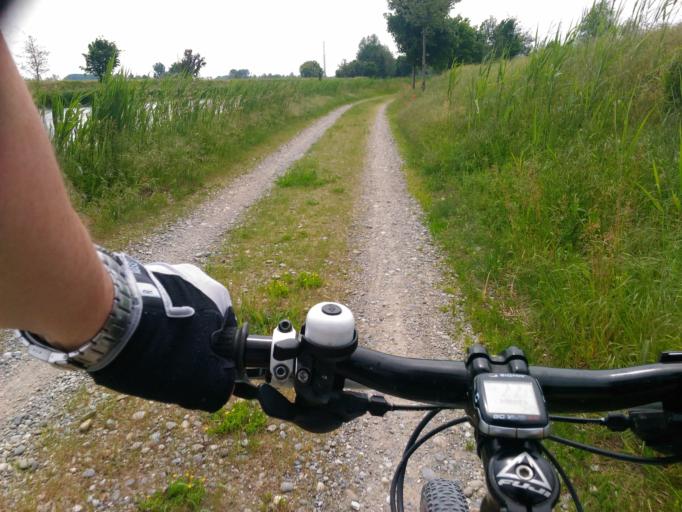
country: IT
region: Lombardy
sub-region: Provincia di Lodi
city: Cervignano d'Adda
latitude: 45.3695
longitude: 9.4151
